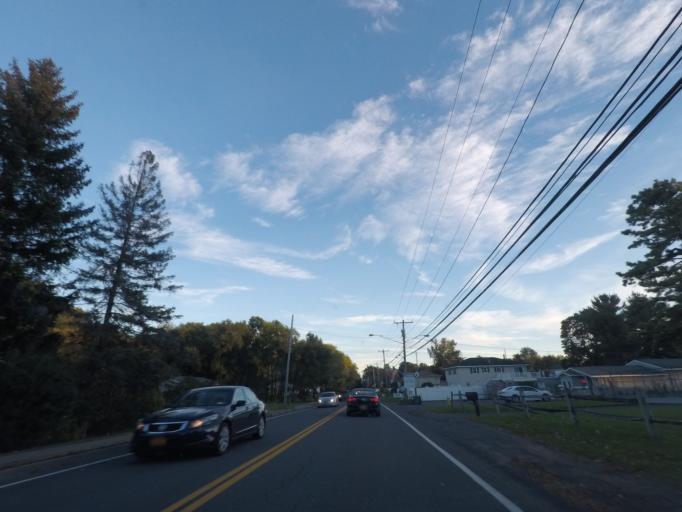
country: US
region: New York
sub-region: Albany County
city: Colonie
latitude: 42.7261
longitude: -73.8236
